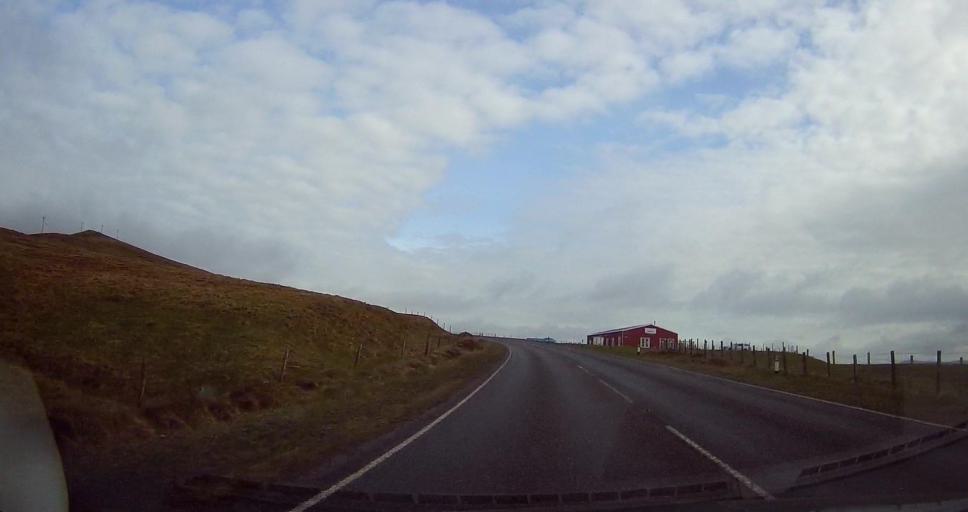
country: GB
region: Scotland
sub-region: Shetland Islands
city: Sandwick
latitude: 60.0613
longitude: -1.2216
